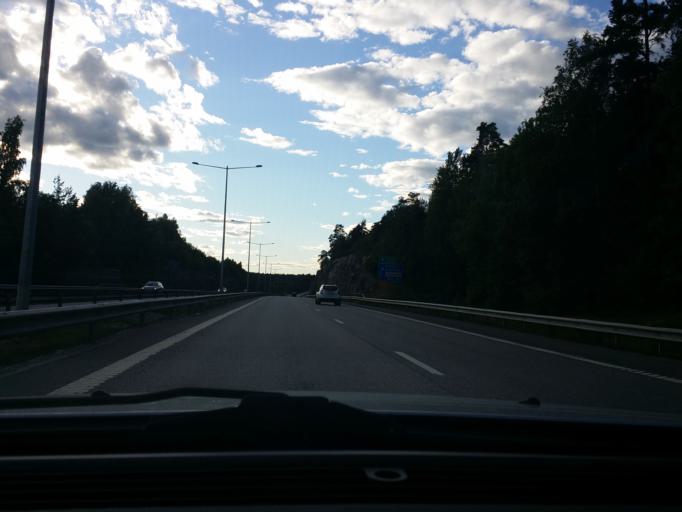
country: SE
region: Stockholm
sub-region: Upplands-Bro Kommun
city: Kungsaengen
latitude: 59.4872
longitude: 17.7566
